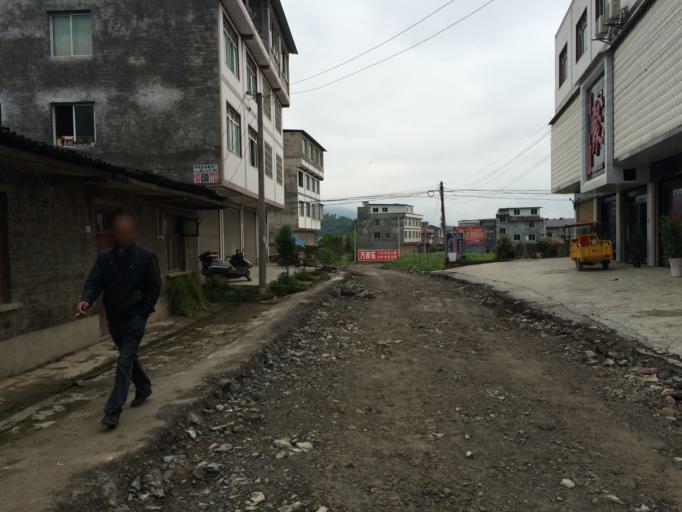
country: CN
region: Guizhou Sheng
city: Dalucao
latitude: 27.8310
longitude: 107.2530
